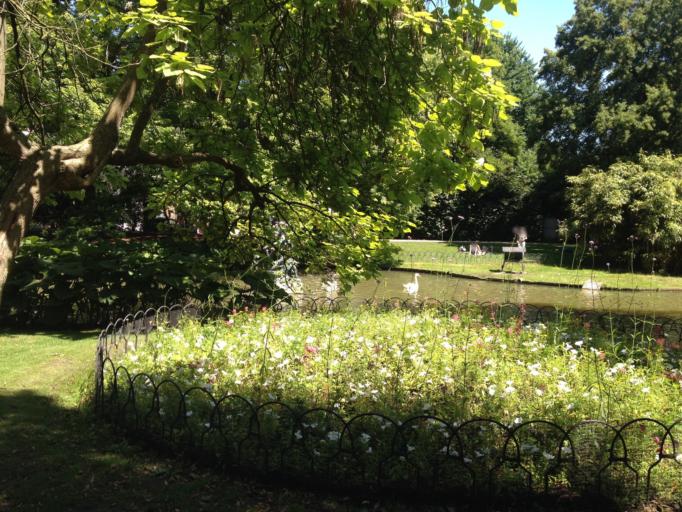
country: BE
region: Flanders
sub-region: Provincie West-Vlaanderen
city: Brugge
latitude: 51.2064
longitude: 3.2311
